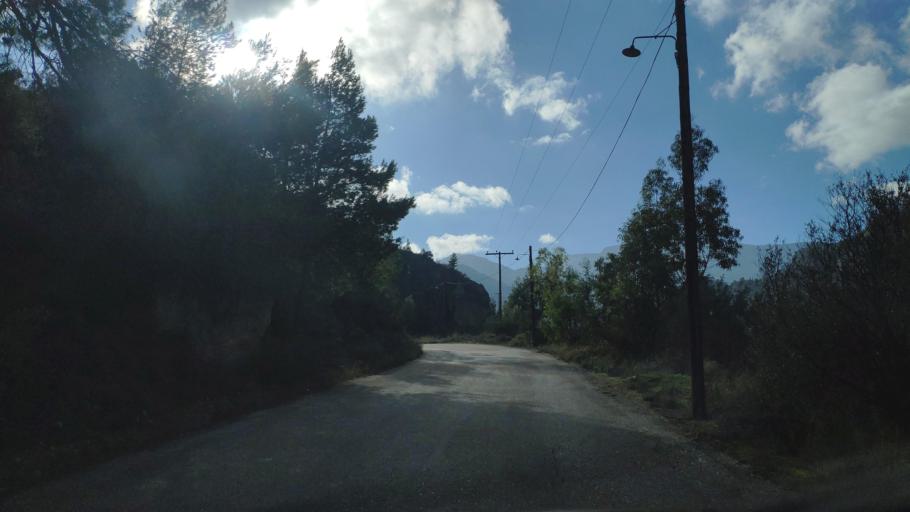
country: GR
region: West Greece
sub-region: Nomos Achaias
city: Aiyira
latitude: 38.1251
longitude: 22.4353
